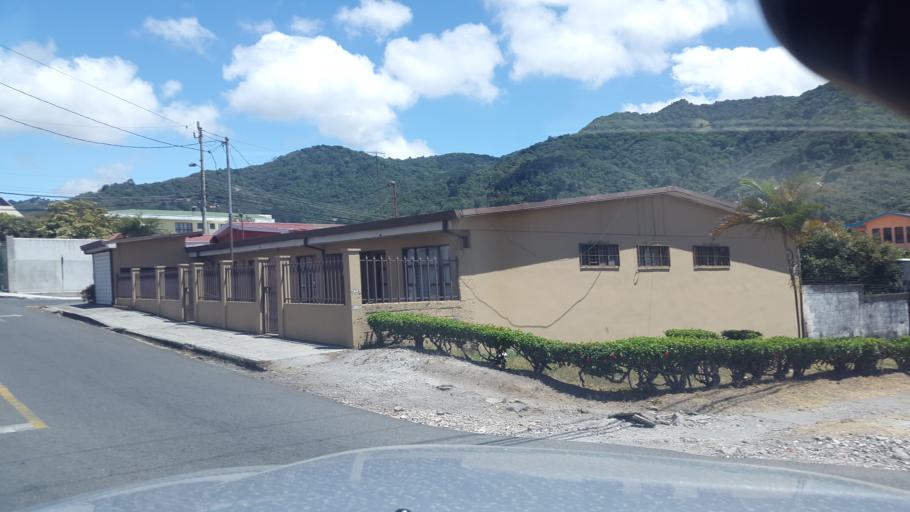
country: CR
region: Cartago
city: Tres Rios
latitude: 9.9053
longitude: -83.9883
